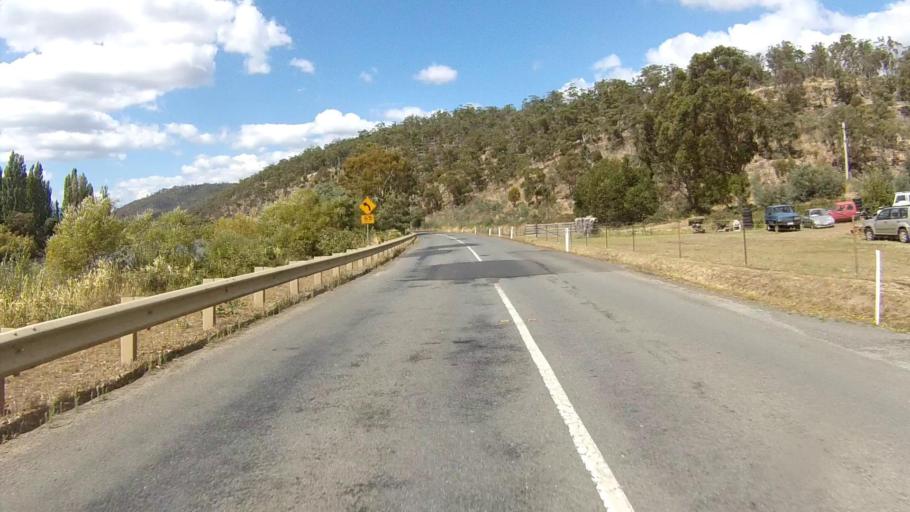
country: AU
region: Tasmania
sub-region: Derwent Valley
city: New Norfolk
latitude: -42.7765
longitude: 147.0285
